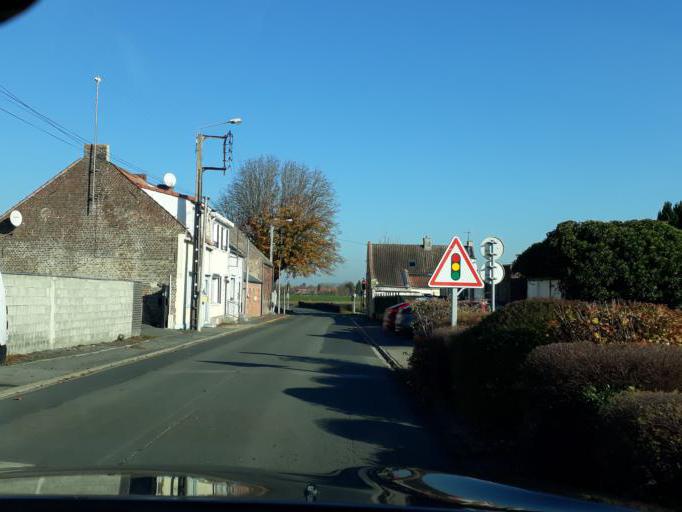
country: FR
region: Nord-Pas-de-Calais
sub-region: Departement du Nord
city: Masny
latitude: 50.3425
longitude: 3.2083
